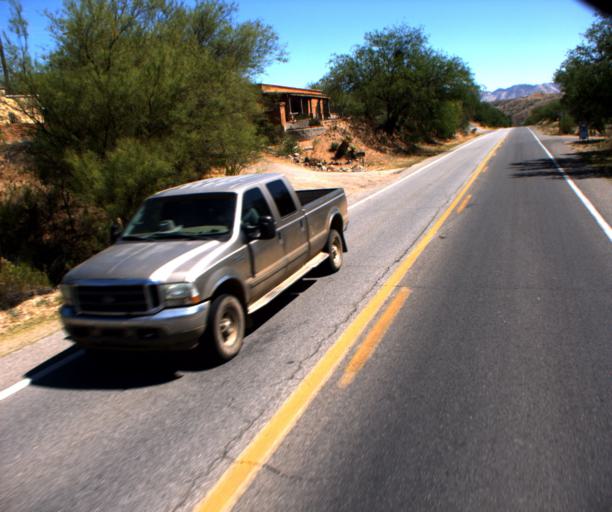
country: US
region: Arizona
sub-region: Santa Cruz County
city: Nogales
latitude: 31.3639
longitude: -110.9044
